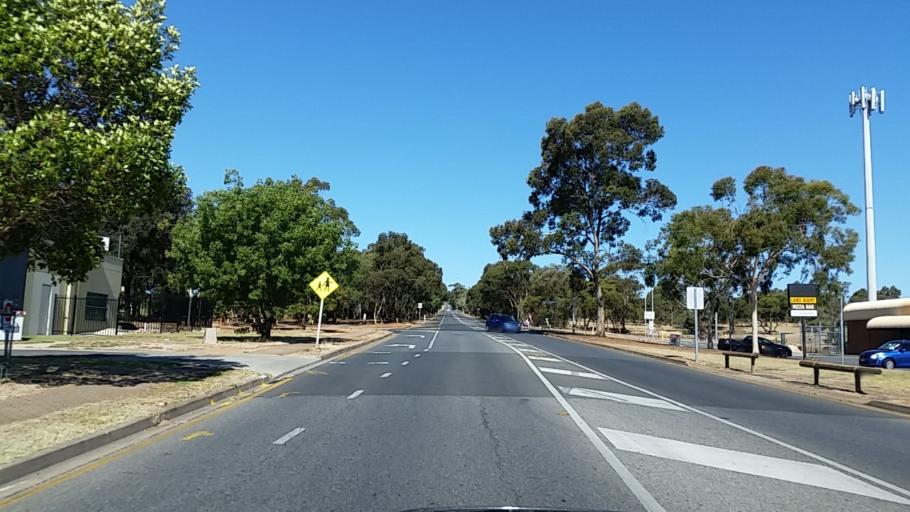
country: AU
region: South Australia
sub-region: Salisbury
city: Elizabeth
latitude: -34.7080
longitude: 138.7066
